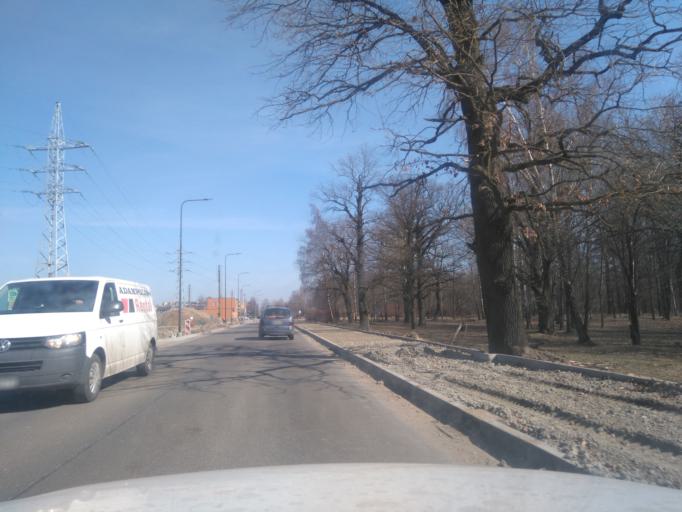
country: LT
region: Kauno apskritis
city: Dainava (Kaunas)
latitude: 54.8827
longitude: 23.9494
